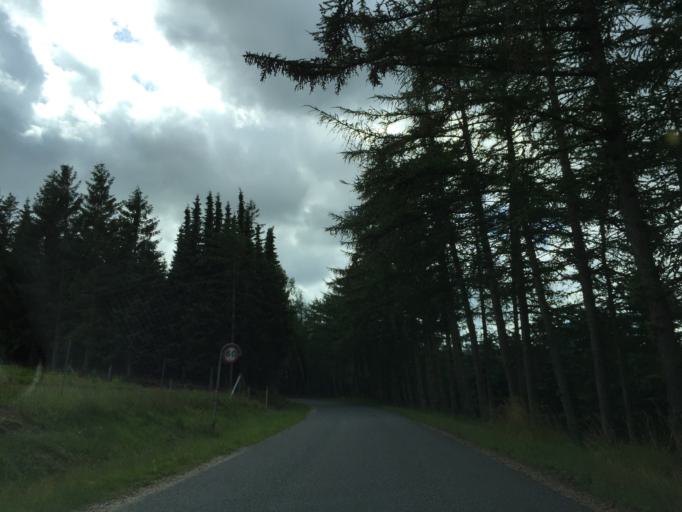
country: DK
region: Central Jutland
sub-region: Silkeborg Kommune
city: Svejbaek
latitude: 56.2085
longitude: 9.7126
